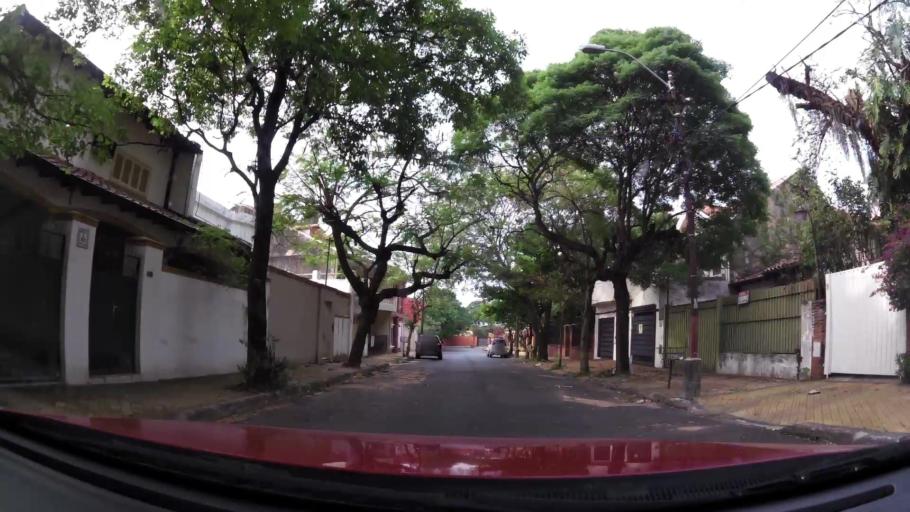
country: PY
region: Asuncion
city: Asuncion
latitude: -25.2915
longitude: -57.6125
